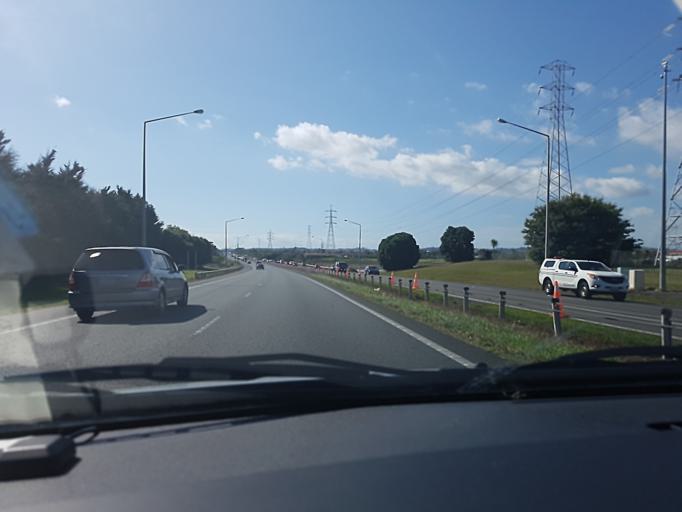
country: NZ
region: Auckland
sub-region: Auckland
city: Papakura
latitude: -37.0620
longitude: 174.9244
